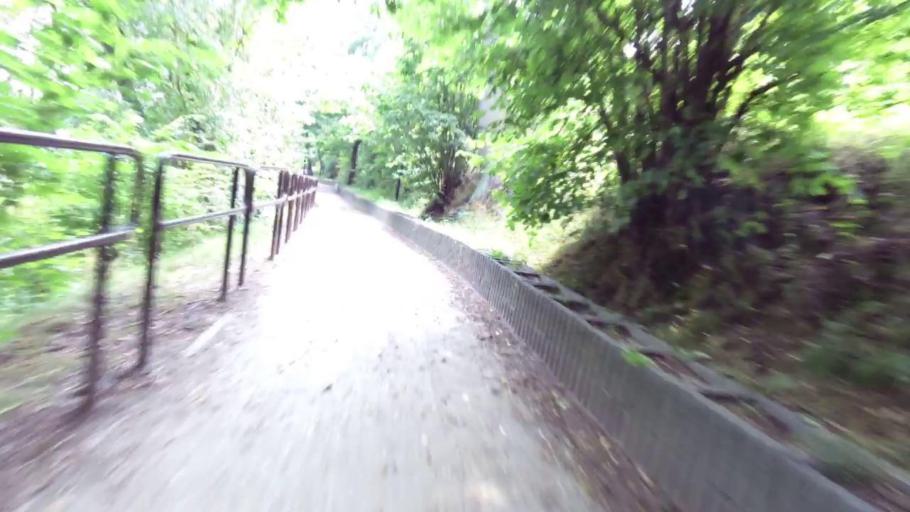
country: PL
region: West Pomeranian Voivodeship
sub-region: Powiat choszczenski
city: Choszczno
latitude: 53.1545
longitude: 15.4275
